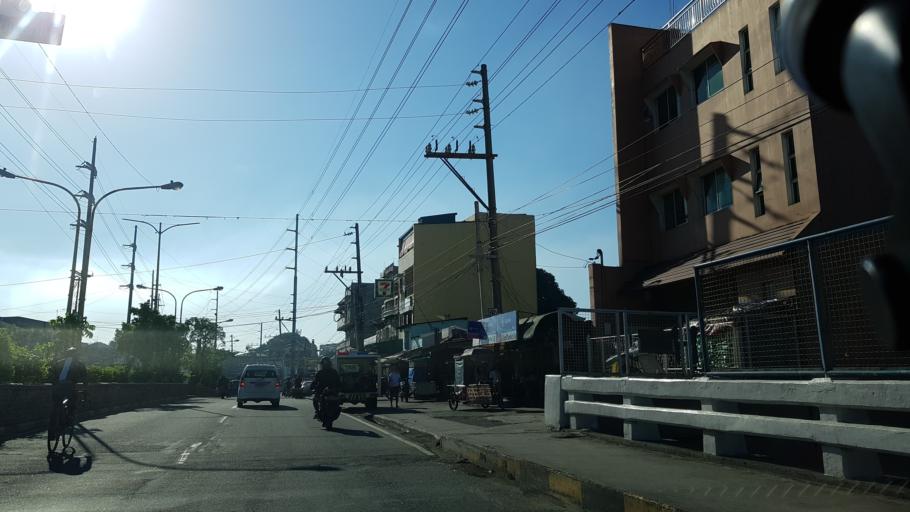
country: PH
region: Calabarzon
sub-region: Province of Rizal
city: Pateros
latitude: 14.5549
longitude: 121.0652
